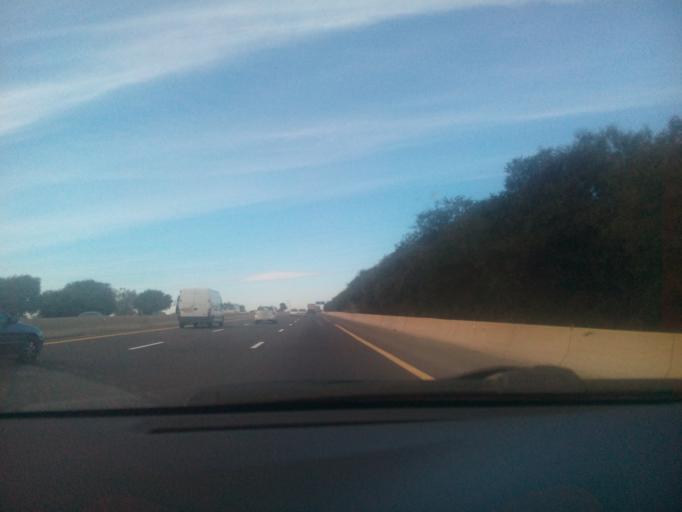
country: DZ
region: Oran
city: Sidi ech Chahmi
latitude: 35.5730
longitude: -0.5459
